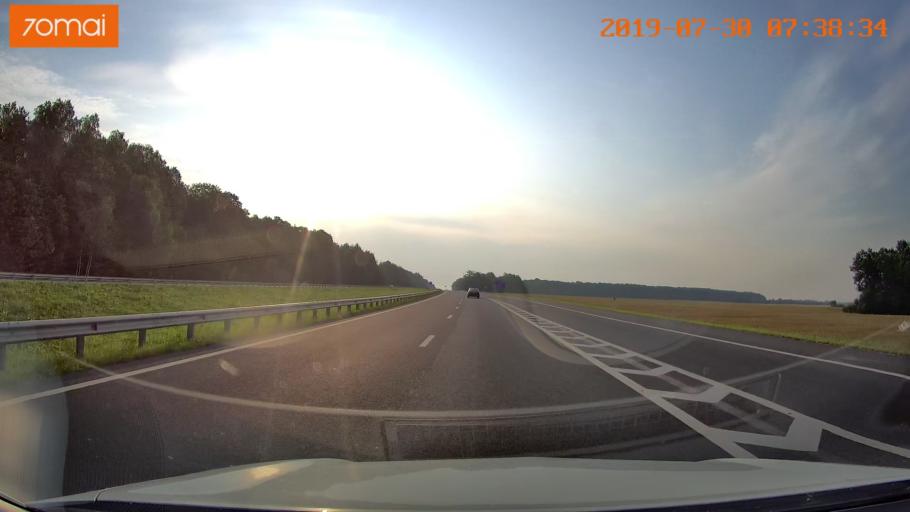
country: RU
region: Kaliningrad
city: Gvardeysk
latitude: 54.6499
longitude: 21.1727
